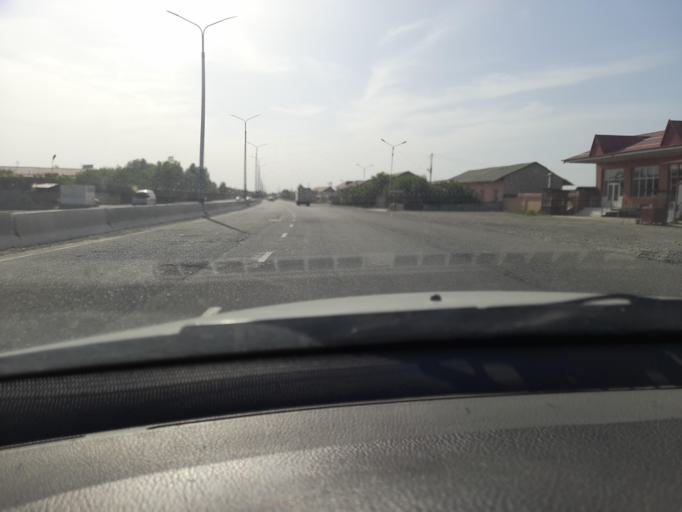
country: UZ
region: Samarqand
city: Kattaqo'rg'on
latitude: 39.9232
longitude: 66.2841
